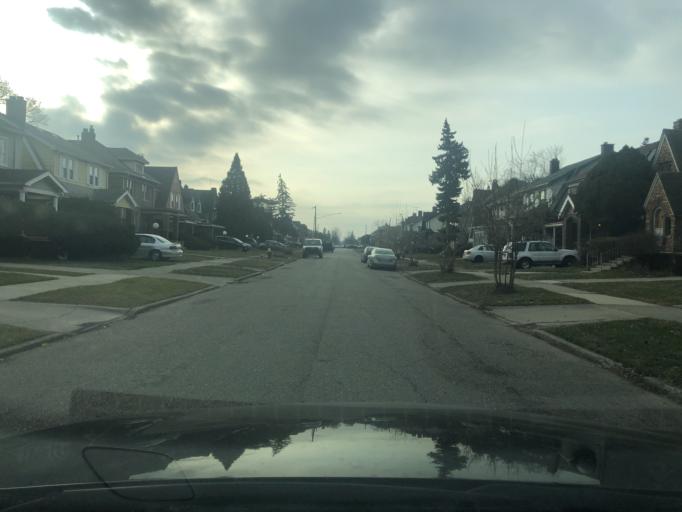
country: US
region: Michigan
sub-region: Wayne County
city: Highland Park
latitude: 42.3882
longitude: -83.1429
